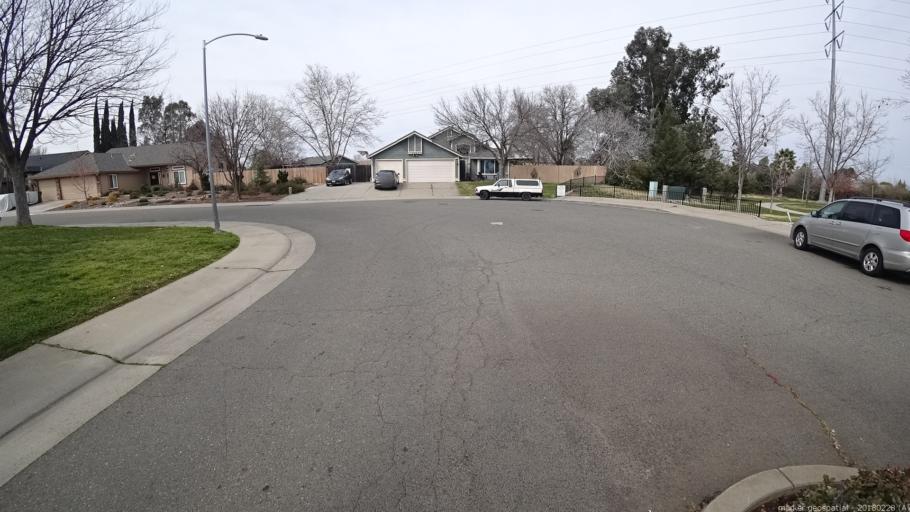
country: US
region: California
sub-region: Sacramento County
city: Antelope
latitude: 38.7063
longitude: -121.3368
